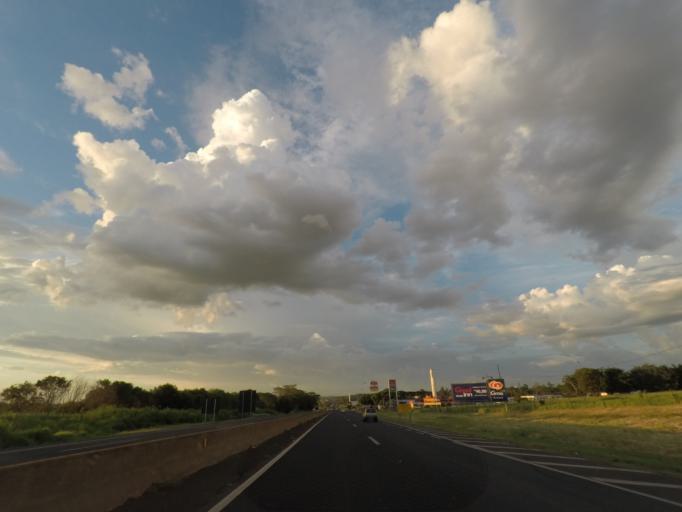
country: BR
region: Minas Gerais
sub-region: Uberaba
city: Uberaba
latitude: -19.7675
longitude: -47.9751
